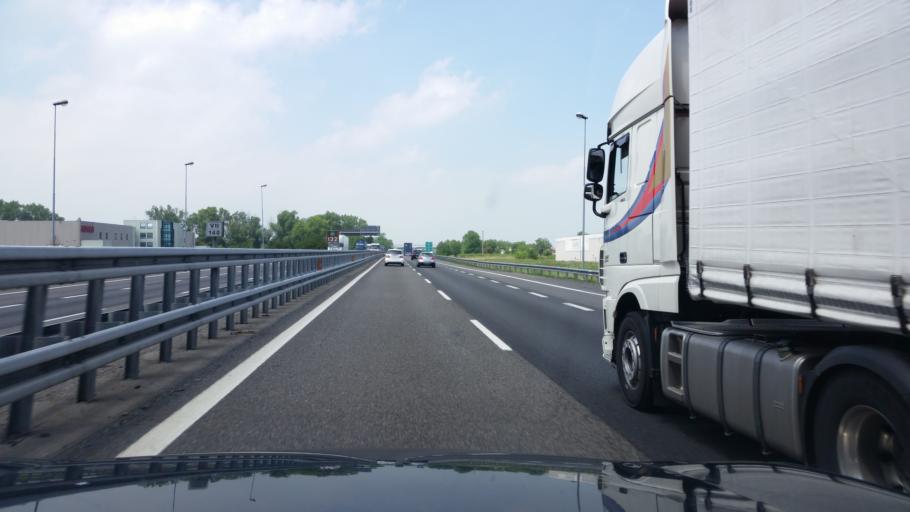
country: IT
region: Emilia-Romagna
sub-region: Provincia di Piacenza
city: Castel San Giovanni
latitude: 45.0759
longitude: 9.4480
